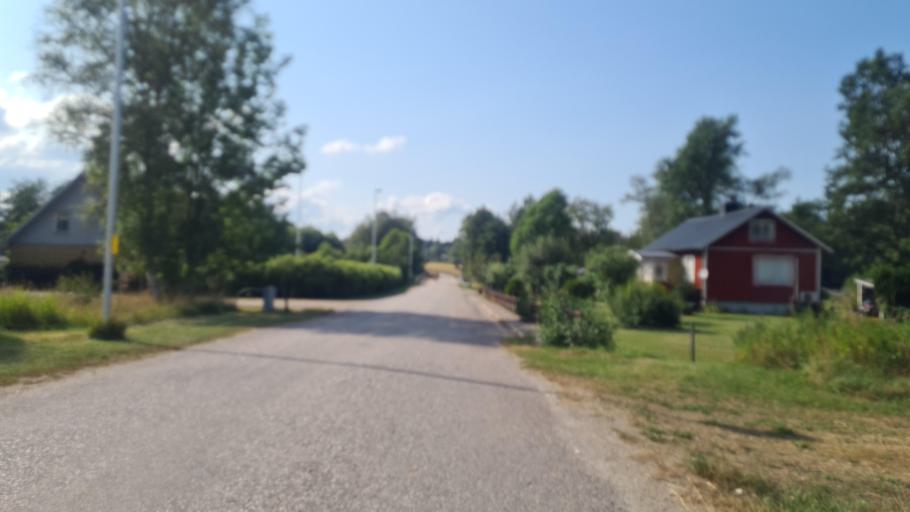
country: SE
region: Kronoberg
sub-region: Ljungby Kommun
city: Ljungby
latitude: 56.7406
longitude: 13.8758
